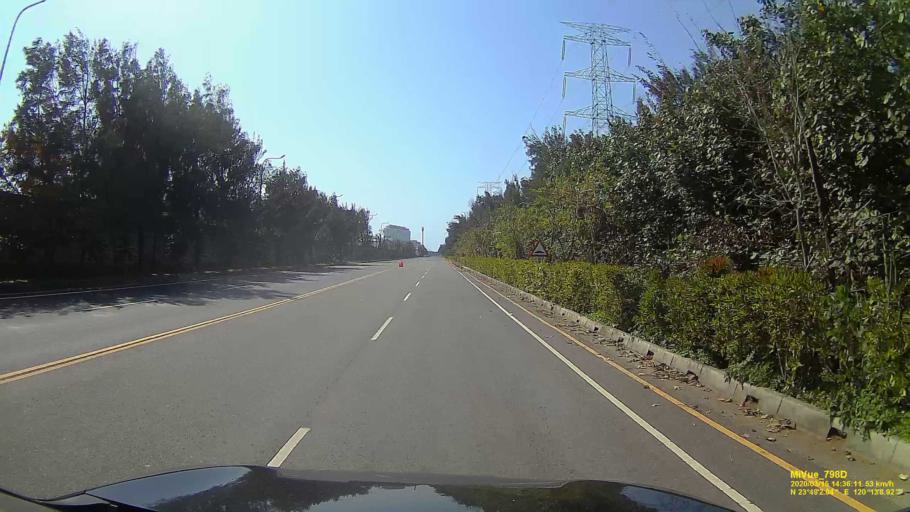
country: TW
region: Taiwan
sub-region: Yunlin
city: Douliu
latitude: 23.8173
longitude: 120.2189
